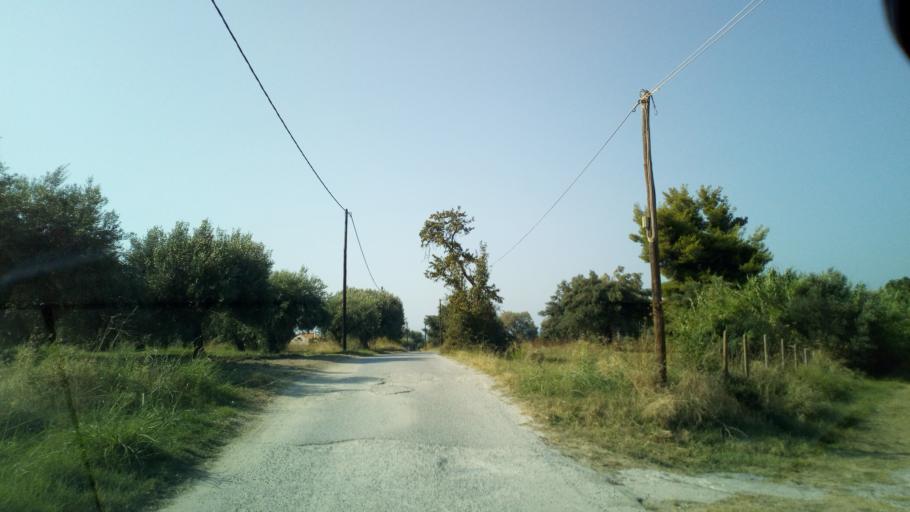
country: GR
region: Central Macedonia
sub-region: Nomos Chalkidikis
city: Pefkochori
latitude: 39.9751
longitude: 23.6523
